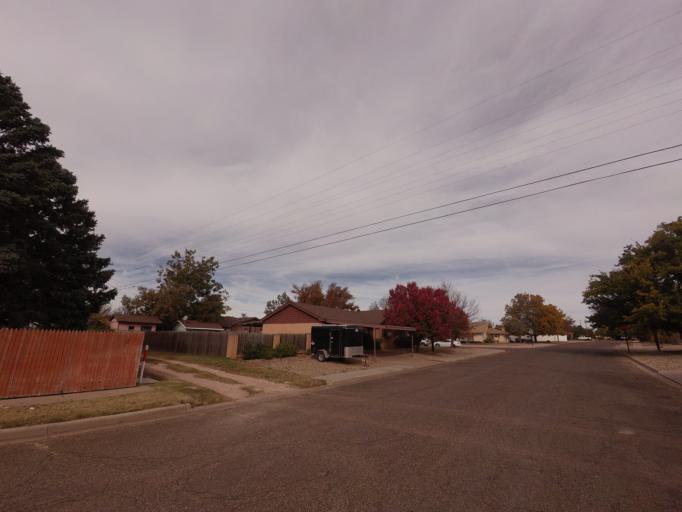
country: US
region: New Mexico
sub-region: Curry County
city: Clovis
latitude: 34.4217
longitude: -103.2116
